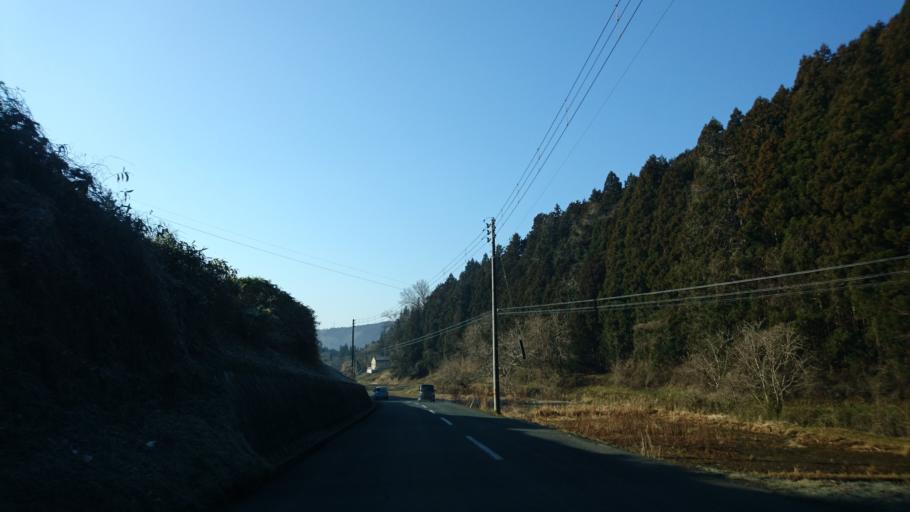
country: JP
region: Iwate
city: Ichinoseki
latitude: 38.9087
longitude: 141.2796
